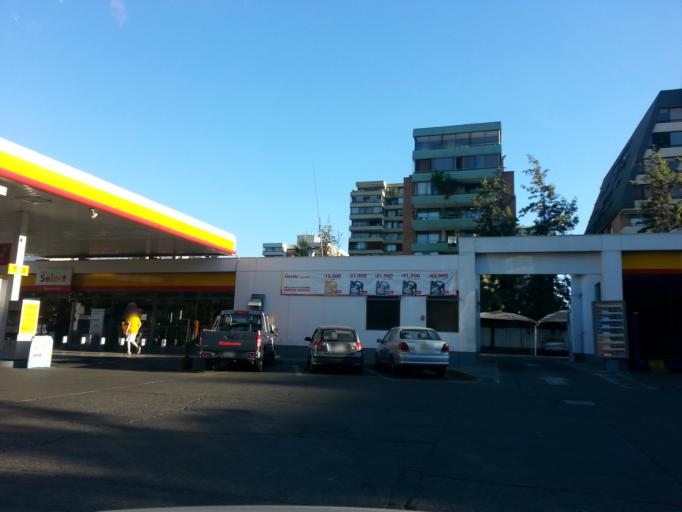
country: CL
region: Santiago Metropolitan
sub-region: Provincia de Santiago
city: Villa Presidente Frei, Nunoa, Santiago, Chile
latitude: -33.4238
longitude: -70.5799
